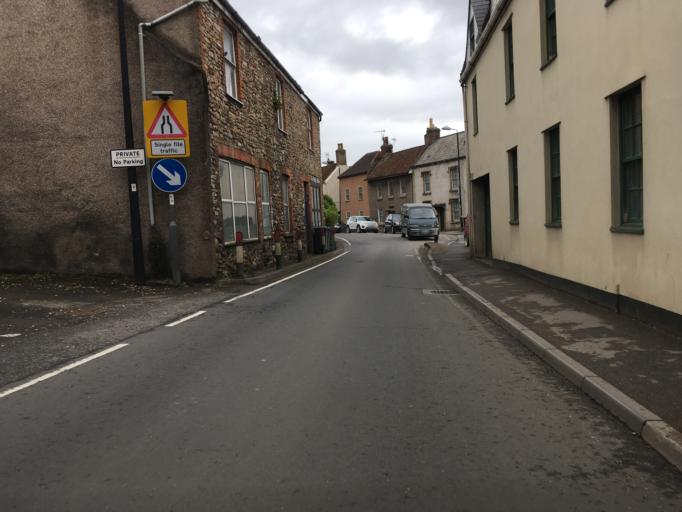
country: GB
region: England
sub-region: North Somerset
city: Banwell
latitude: 51.3279
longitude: -2.8650
